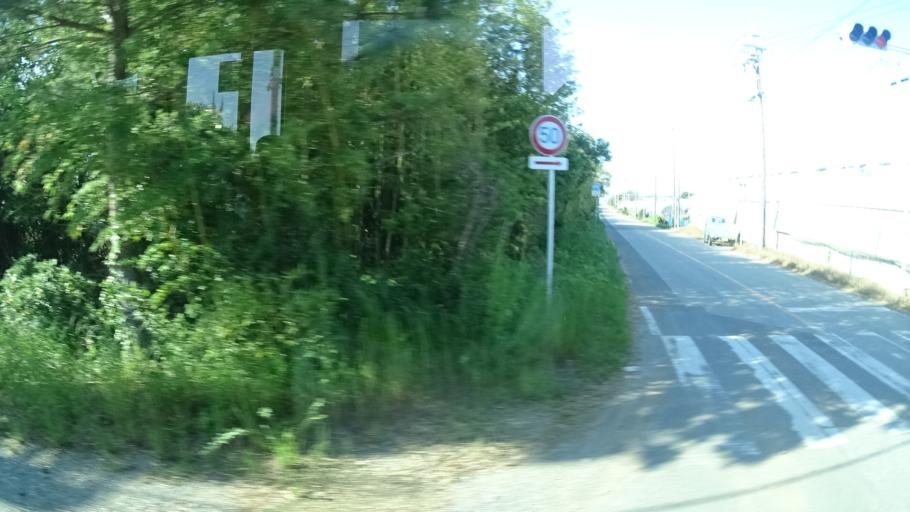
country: JP
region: Aichi
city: Toyohama
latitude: 34.5895
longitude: 137.0415
